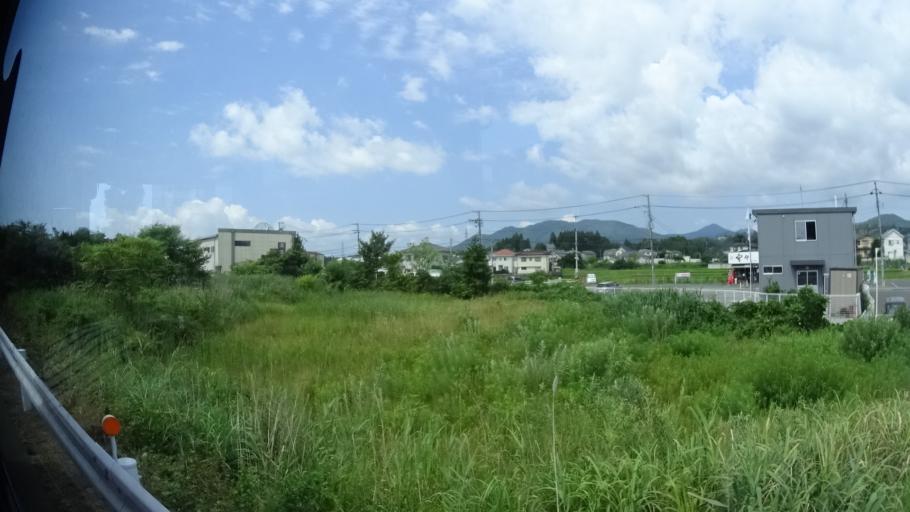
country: JP
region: Iwate
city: Ofunato
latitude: 38.8418
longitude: 141.5812
